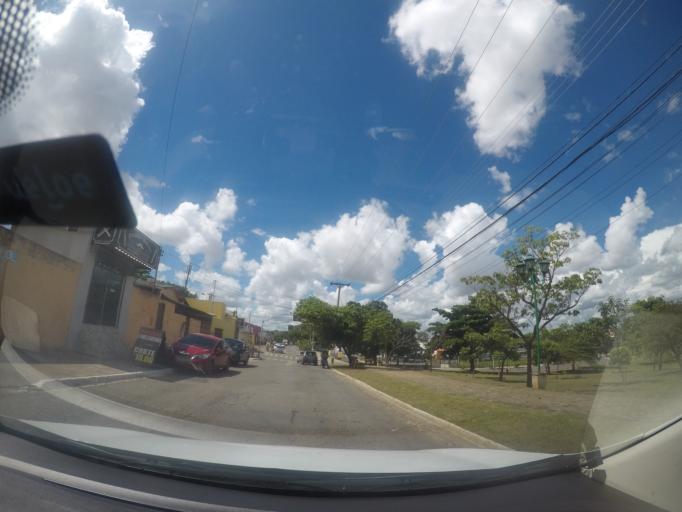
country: BR
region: Goias
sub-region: Goiania
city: Goiania
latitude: -16.6644
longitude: -49.2990
